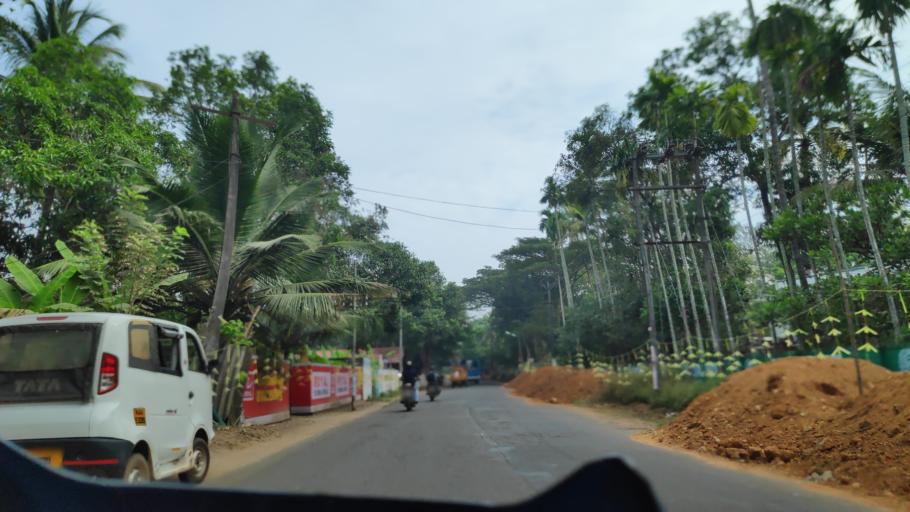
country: IN
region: Kerala
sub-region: Alappuzha
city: Vayalar
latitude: 9.7116
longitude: 76.3581
